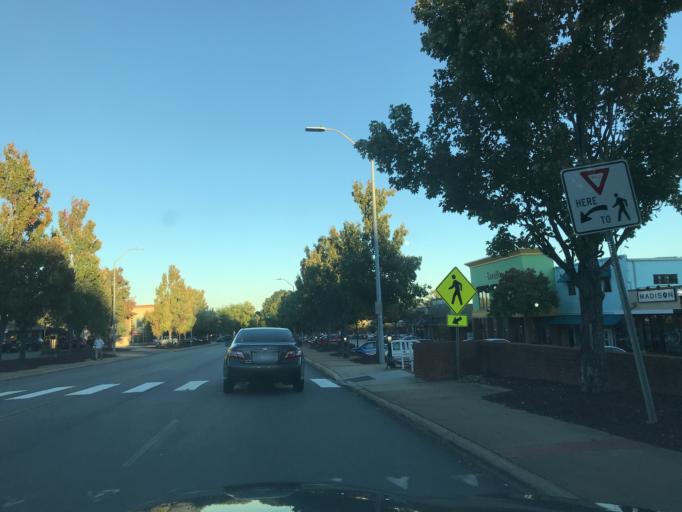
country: US
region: North Carolina
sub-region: Wake County
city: West Raleigh
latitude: 35.7909
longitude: -78.6610
